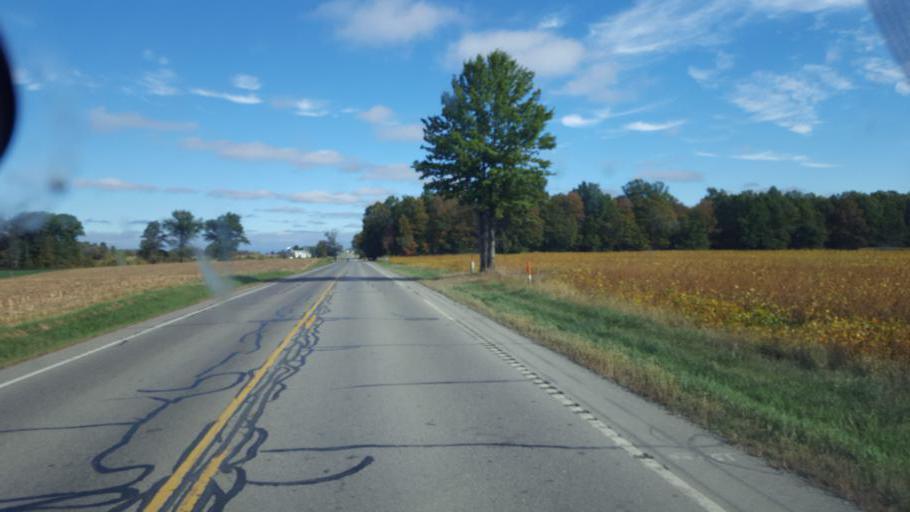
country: US
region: Ohio
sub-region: Huron County
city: Greenwich
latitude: 40.9801
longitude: -82.4906
